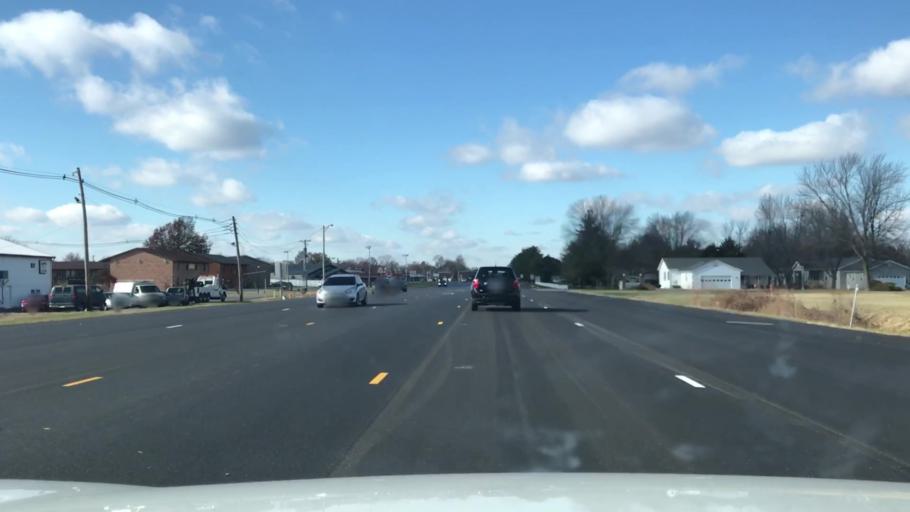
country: US
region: Illinois
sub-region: Saint Clair County
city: Swansea
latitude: 38.5481
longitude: -90.0055
